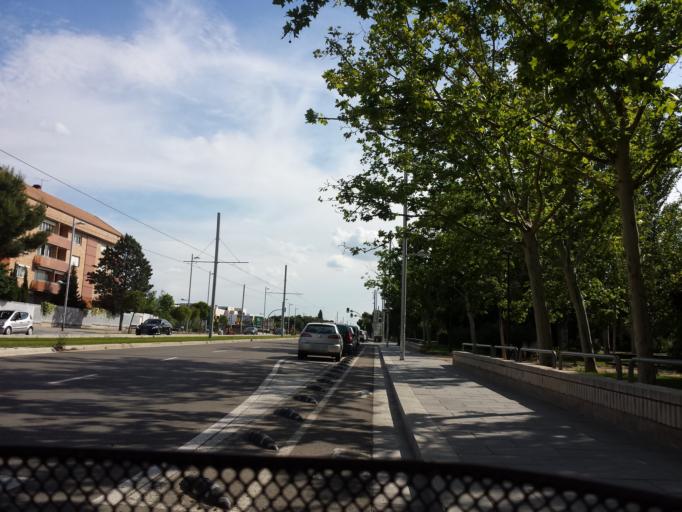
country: ES
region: Aragon
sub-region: Provincia de Zaragoza
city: Delicias
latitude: 41.6294
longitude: -0.9073
